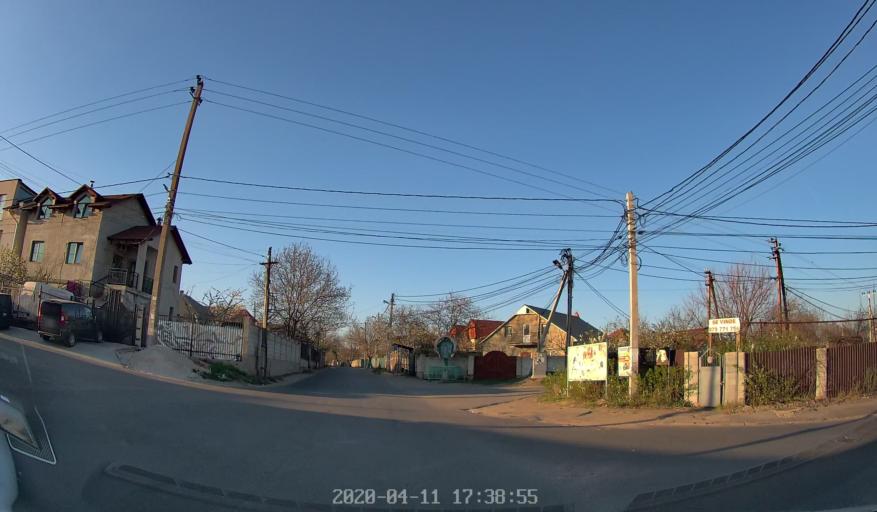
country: MD
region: Laloveni
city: Ialoveni
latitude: 46.9848
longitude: 28.8042
